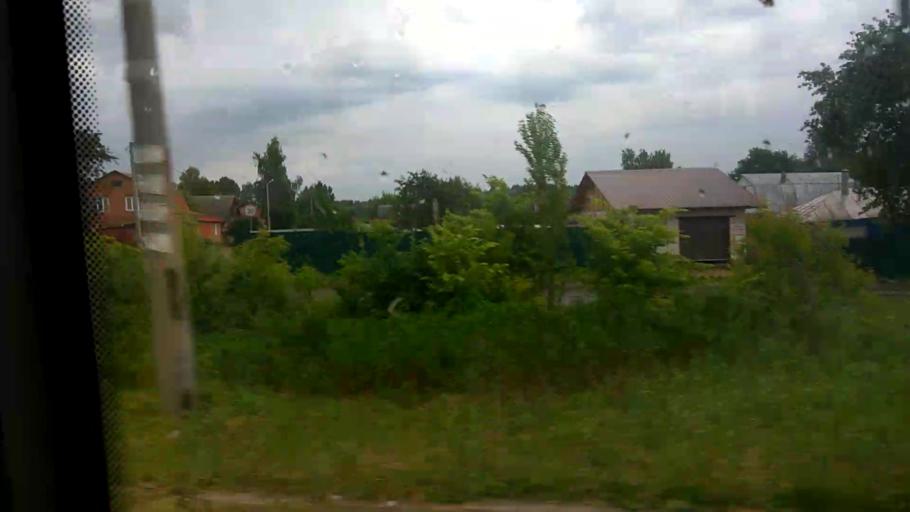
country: RU
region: Moskovskaya
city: Zaraysk
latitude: 54.7573
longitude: 38.8583
